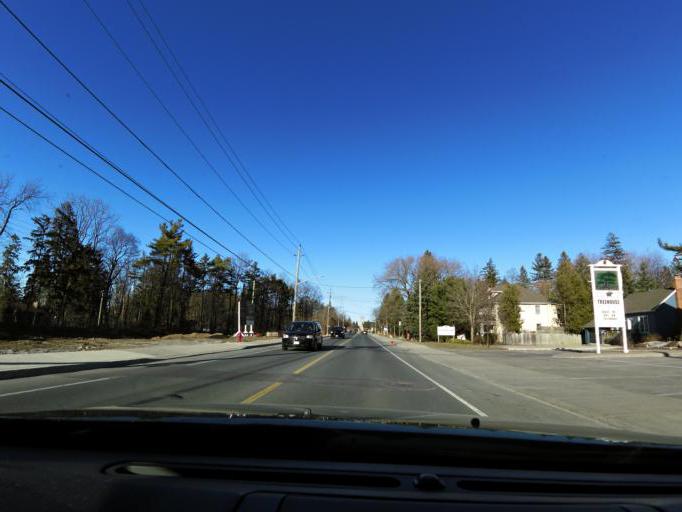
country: CA
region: Ontario
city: Ancaster
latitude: 43.2209
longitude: -79.9824
